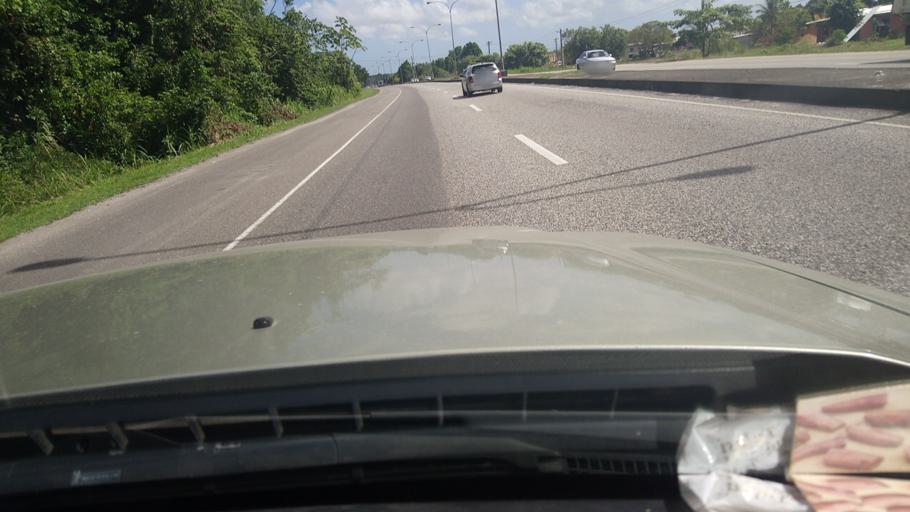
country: TT
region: Borough of Arima
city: Arima
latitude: 10.6295
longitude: -61.2361
